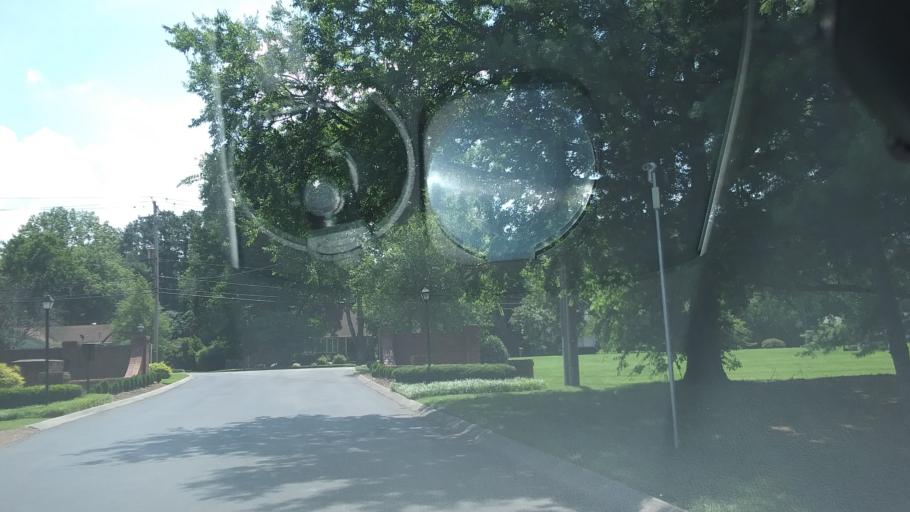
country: US
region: Tennessee
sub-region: Davidson County
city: Belle Meade
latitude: 36.0844
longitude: -86.9445
